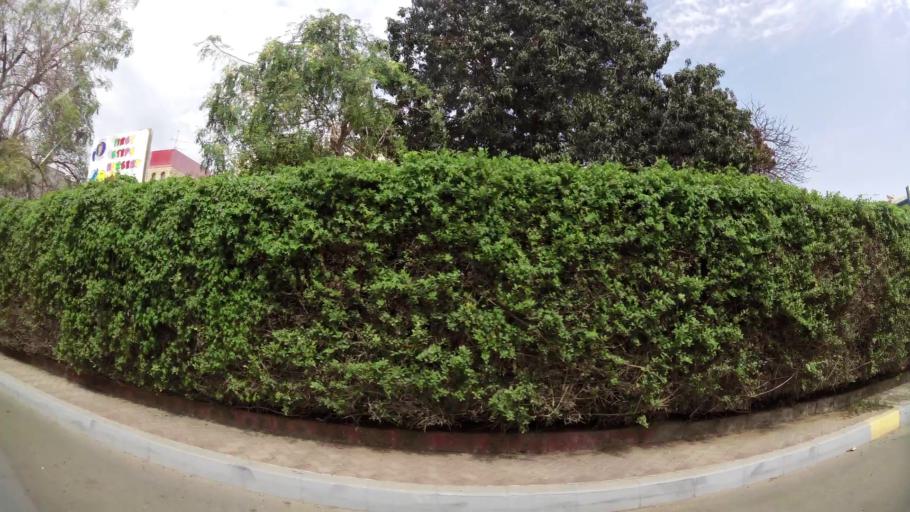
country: AE
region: Abu Dhabi
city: Abu Dhabi
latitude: 24.4600
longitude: 54.3686
